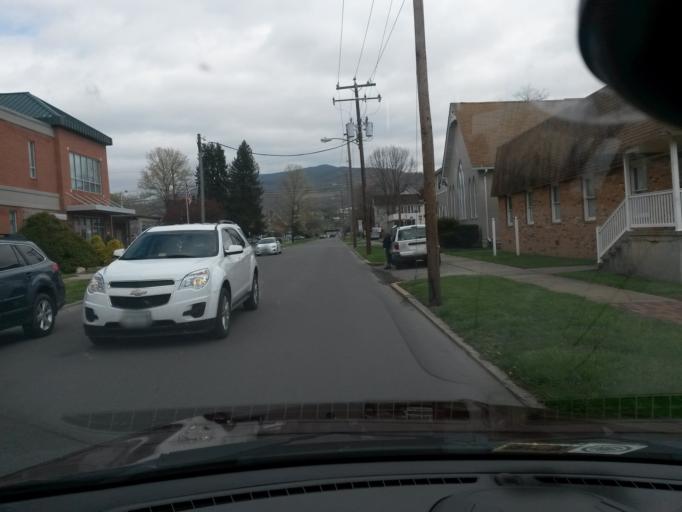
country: US
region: Virginia
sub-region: City of Covington
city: Covington
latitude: 37.7917
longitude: -79.9983
